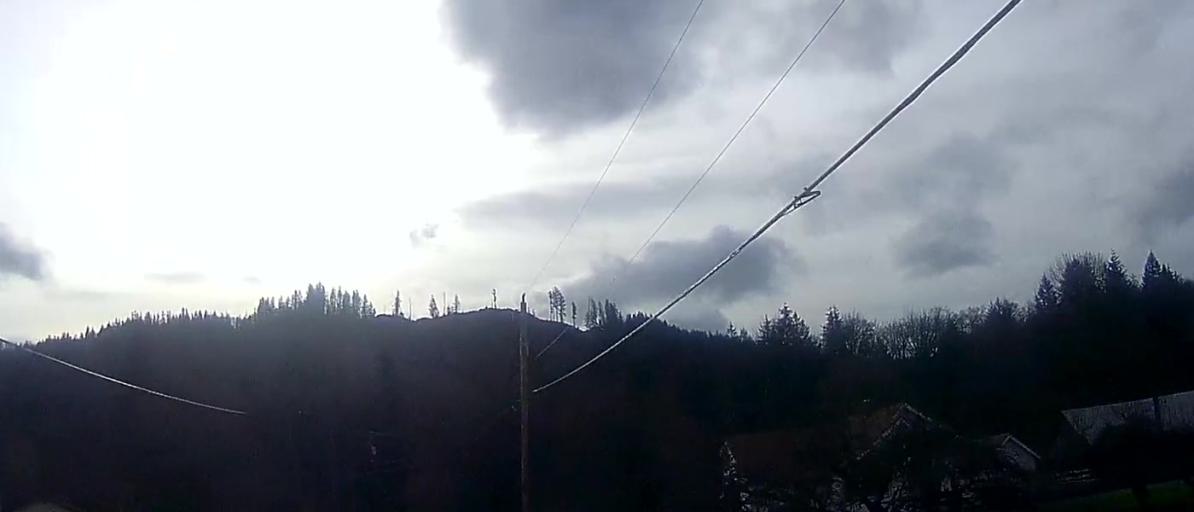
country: US
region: Washington
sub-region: Skagit County
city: Sedro-Woolley
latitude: 48.5590
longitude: -122.2912
